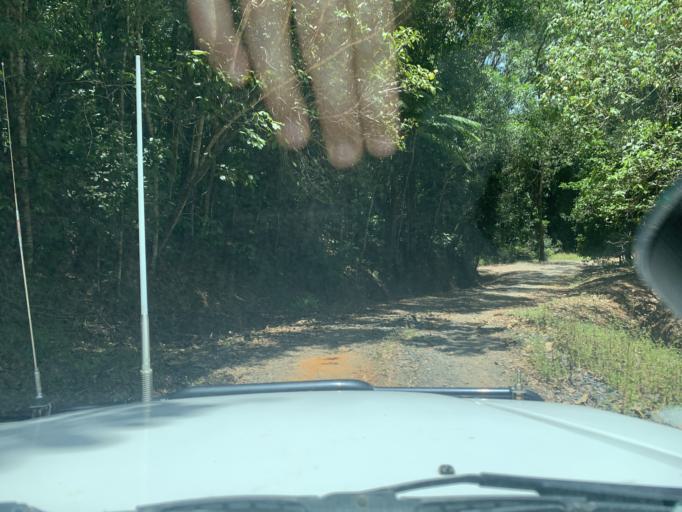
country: AU
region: Queensland
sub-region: Cairns
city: Woree
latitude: -16.9762
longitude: 145.6510
